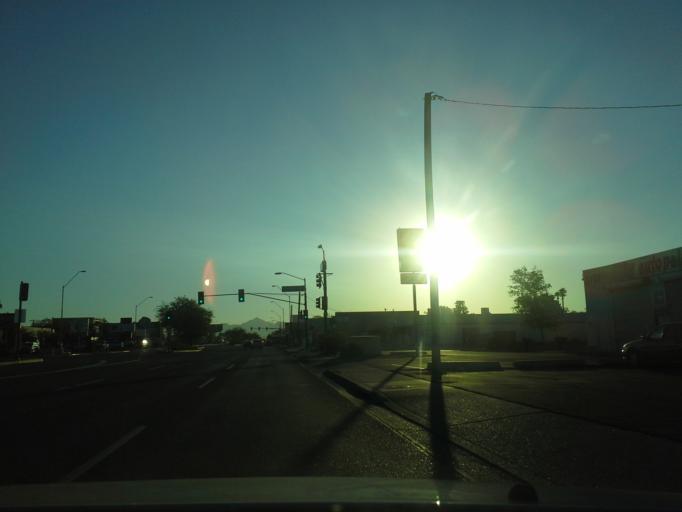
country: US
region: Arizona
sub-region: Maricopa County
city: Paradise Valley
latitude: 33.6405
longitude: -112.0229
